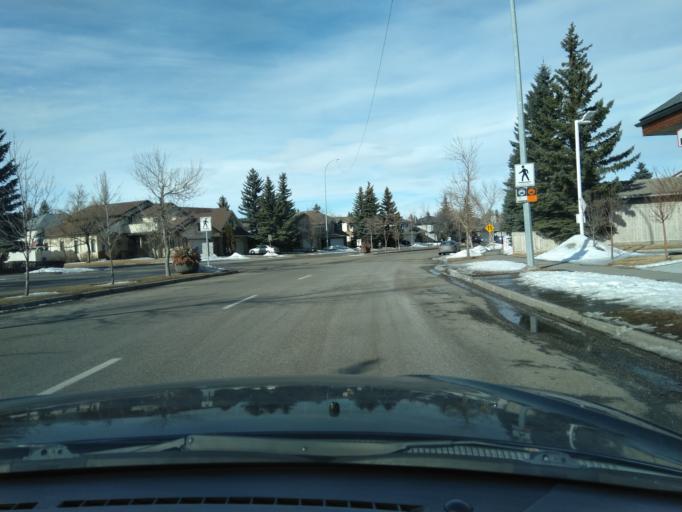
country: CA
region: Alberta
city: Calgary
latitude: 51.1283
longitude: -114.1385
